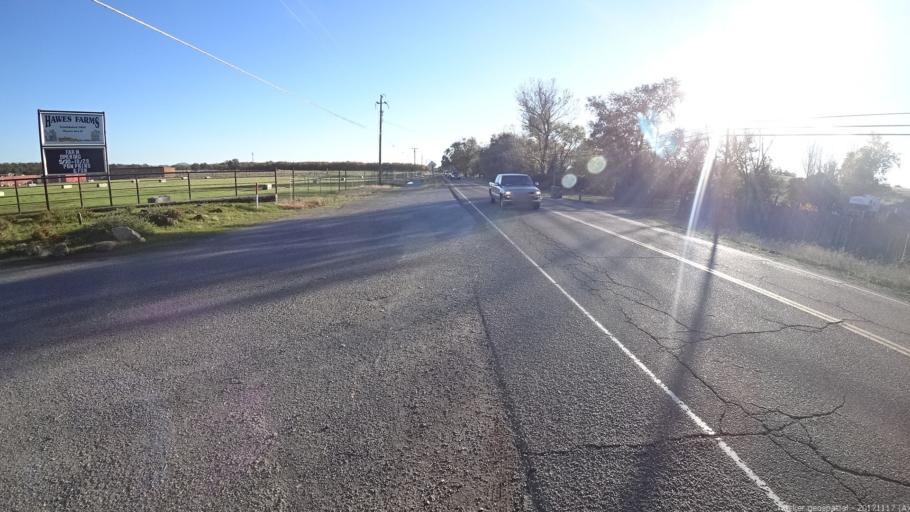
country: US
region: California
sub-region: Shasta County
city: Anderson
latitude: 40.4755
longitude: -122.2415
